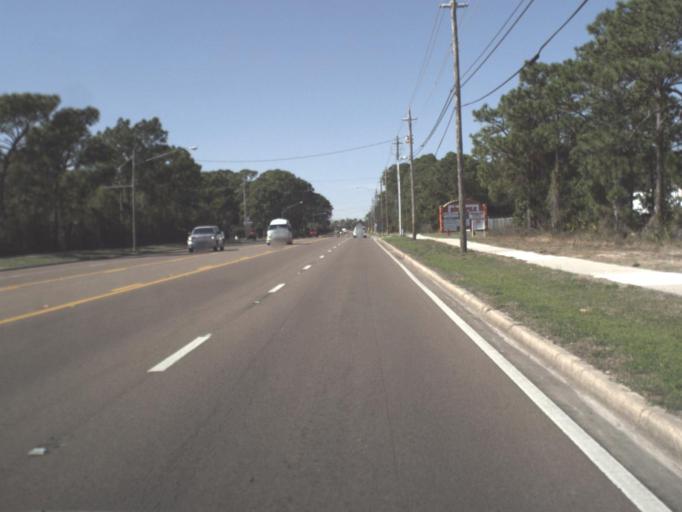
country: US
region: Florida
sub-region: Bay County
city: Panama City Beach
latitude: 30.1943
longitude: -85.8266
